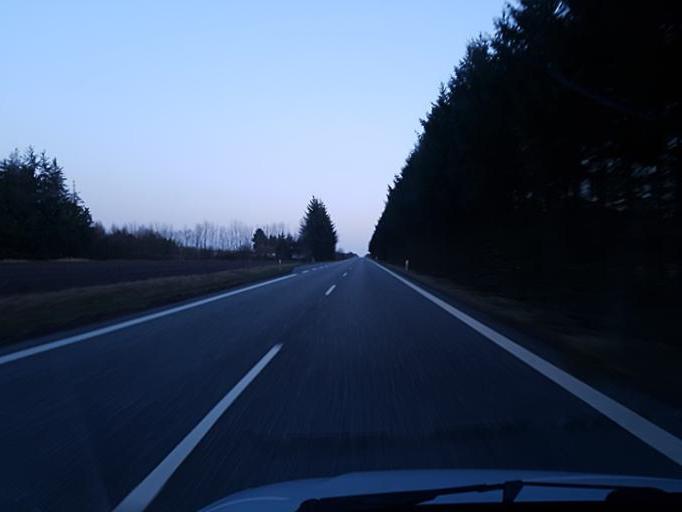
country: DK
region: Central Jutland
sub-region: Holstebro Kommune
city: Holstebro
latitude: 56.2642
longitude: 8.6058
